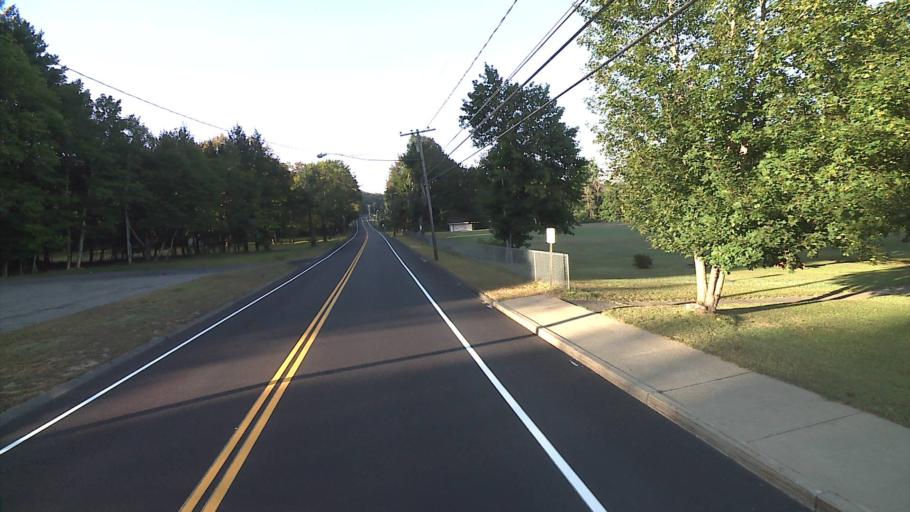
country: US
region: Connecticut
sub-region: Tolland County
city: Storrs
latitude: 41.8509
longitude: -72.3020
